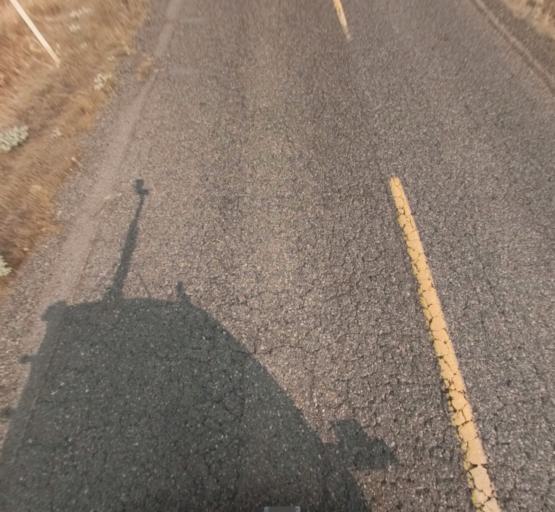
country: US
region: California
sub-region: Madera County
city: Bonadelle Ranchos-Madera Ranchos
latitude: 37.1026
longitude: -119.8859
